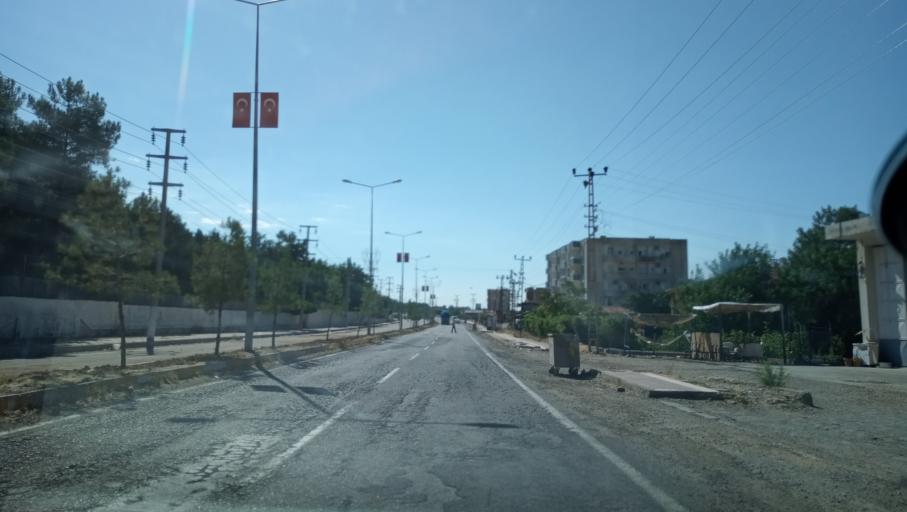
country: TR
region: Diyarbakir
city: Silvan
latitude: 38.1372
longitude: 41.0225
